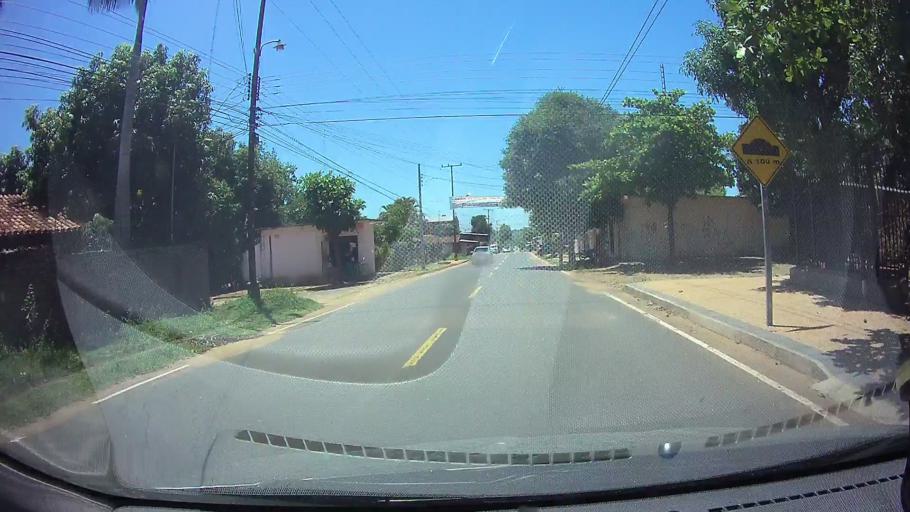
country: PY
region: Central
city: San Lorenzo
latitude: -25.3187
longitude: -57.4914
